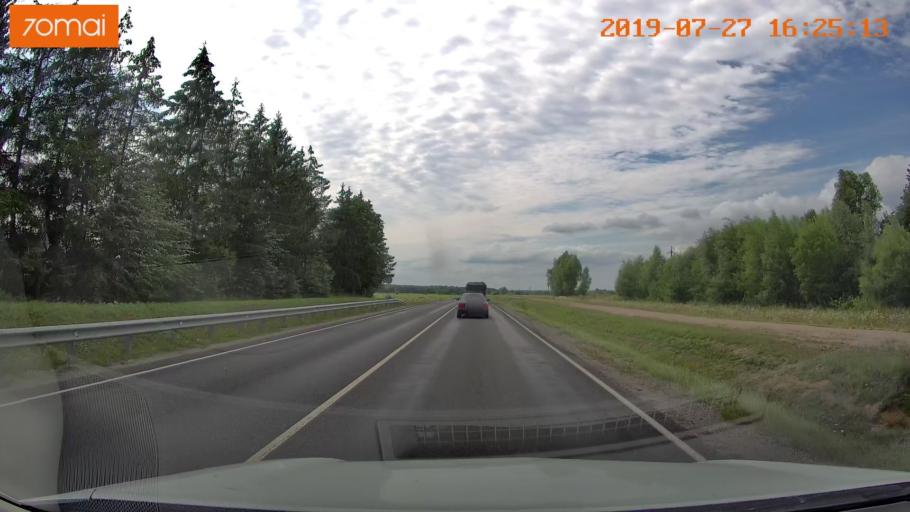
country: RU
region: Kaliningrad
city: Zheleznodorozhnyy
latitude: 54.6366
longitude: 21.4358
